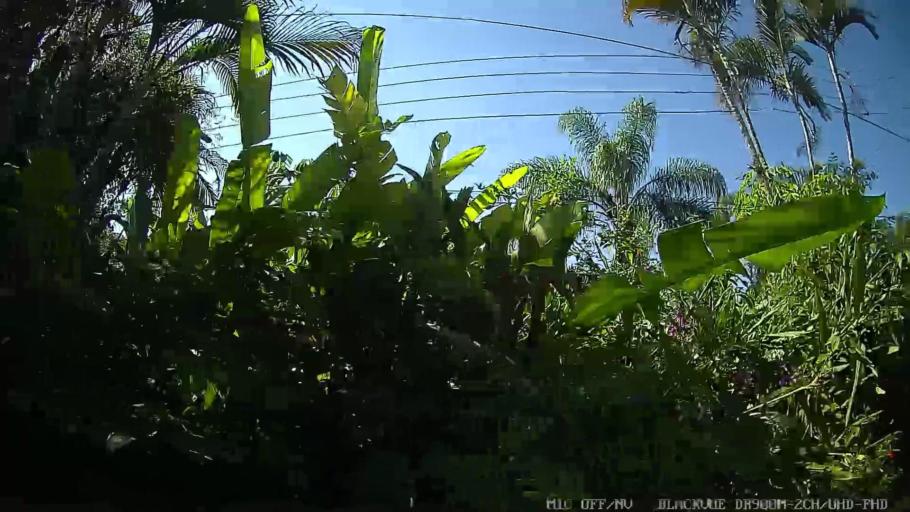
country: BR
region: Sao Paulo
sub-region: Itanhaem
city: Itanhaem
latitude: -24.1436
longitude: -46.7355
